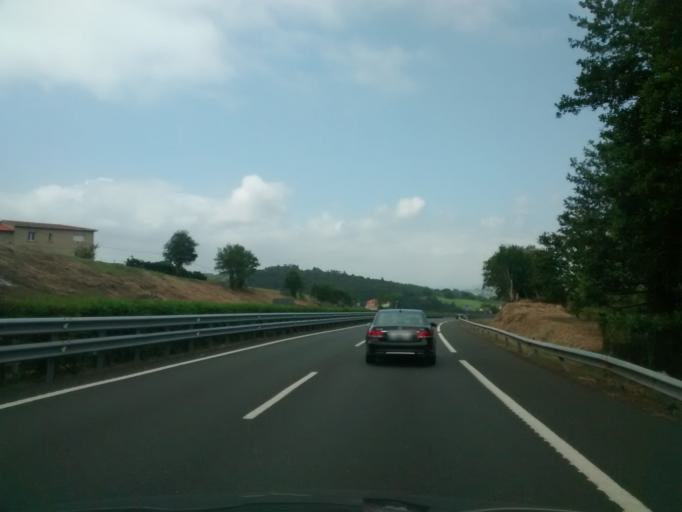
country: ES
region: Cantabria
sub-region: Provincia de Cantabria
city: Santa Cruz de Bezana
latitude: 43.4256
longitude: -3.9352
